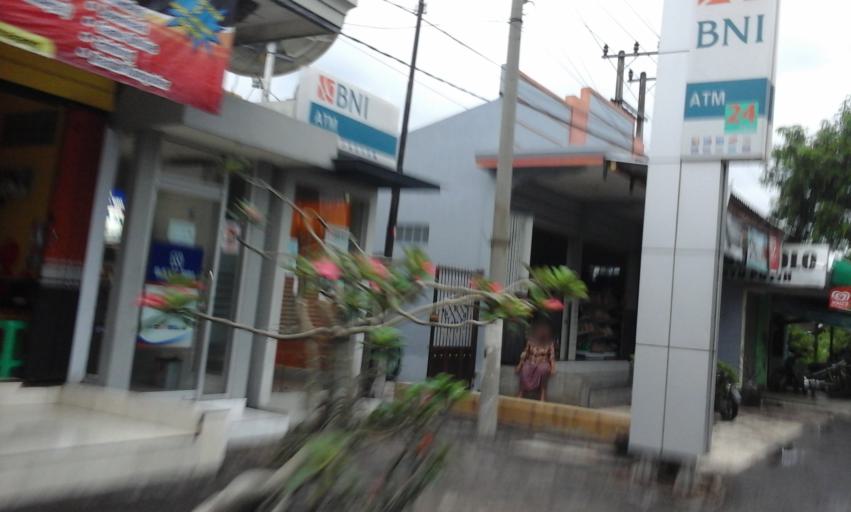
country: ID
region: East Java
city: Pondoktelo
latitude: -8.1101
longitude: 113.2778
